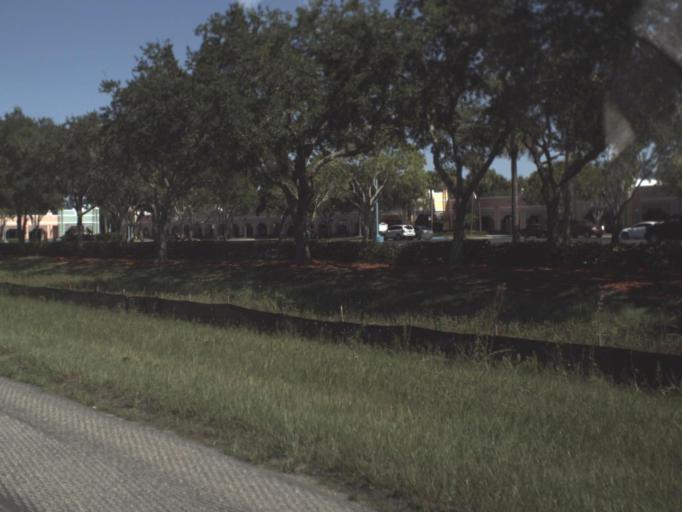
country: US
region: Florida
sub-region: Collier County
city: Lely Resort
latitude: 26.0448
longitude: -81.7000
